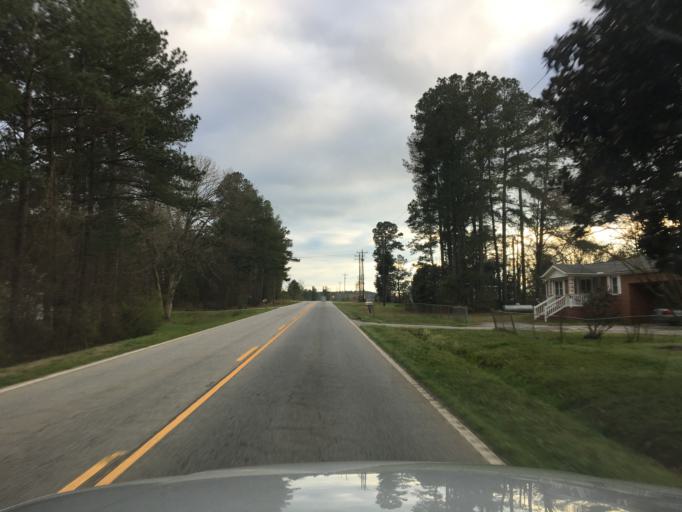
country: US
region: South Carolina
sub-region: Saluda County
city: Saluda
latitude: 33.9722
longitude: -81.7780
